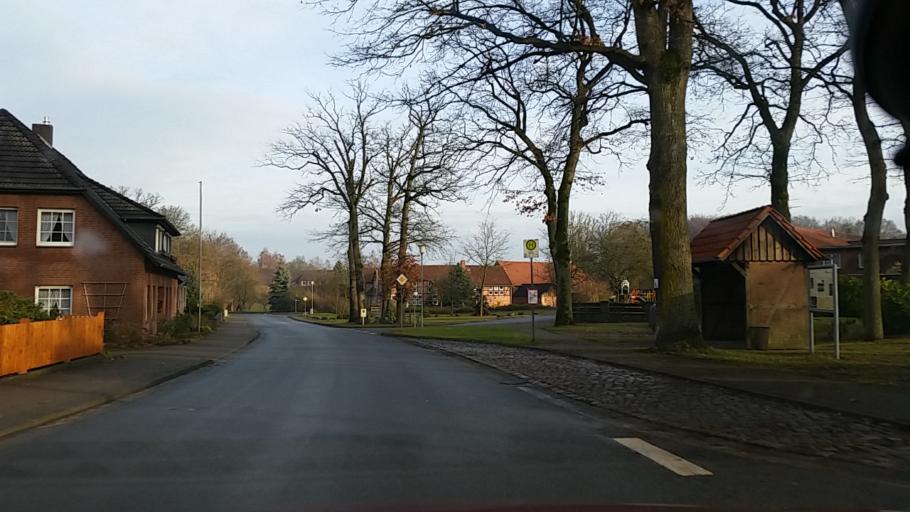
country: DE
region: Lower Saxony
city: Luder
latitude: 52.8109
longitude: 10.6682
